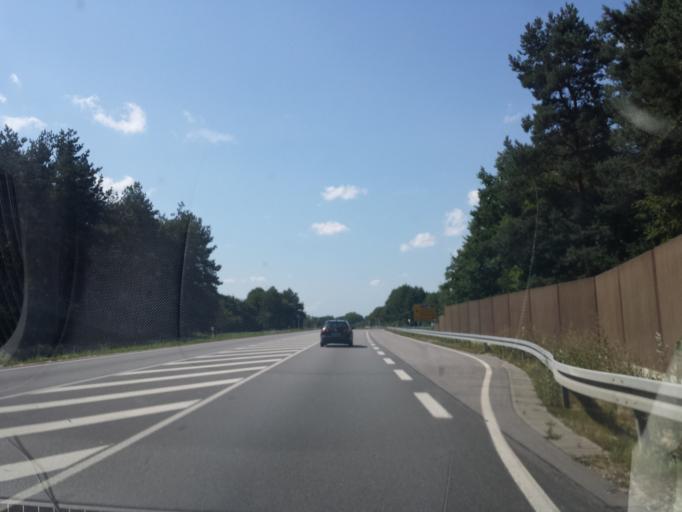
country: DE
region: Bavaria
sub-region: Upper Bavaria
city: Ernsgaden
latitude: 48.7277
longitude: 11.5647
